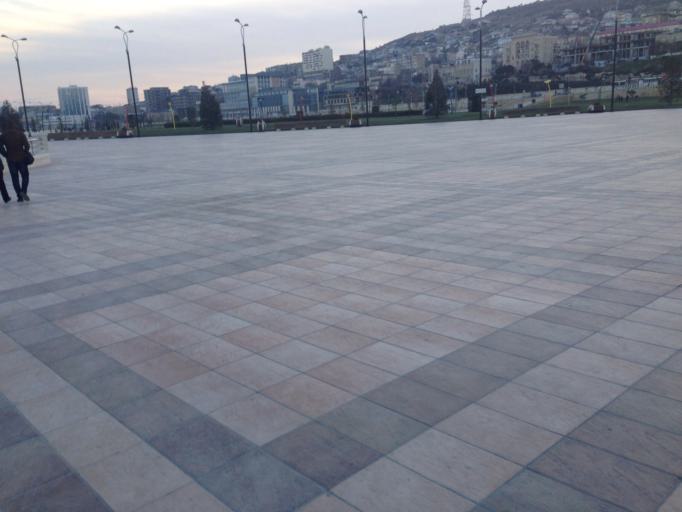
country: AZ
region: Baki
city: Badamdar
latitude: 40.3545
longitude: 49.8358
